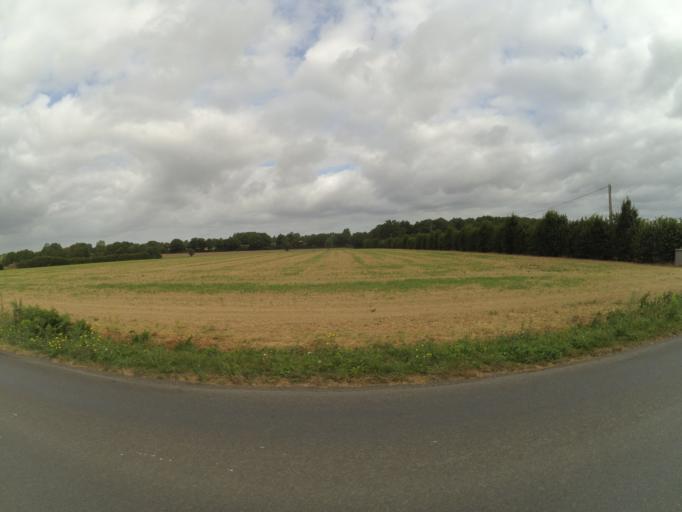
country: FR
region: Pays de la Loire
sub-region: Departement de Maine-et-Loire
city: Villedieu-la-Blouere
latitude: 47.1390
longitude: -1.0739
